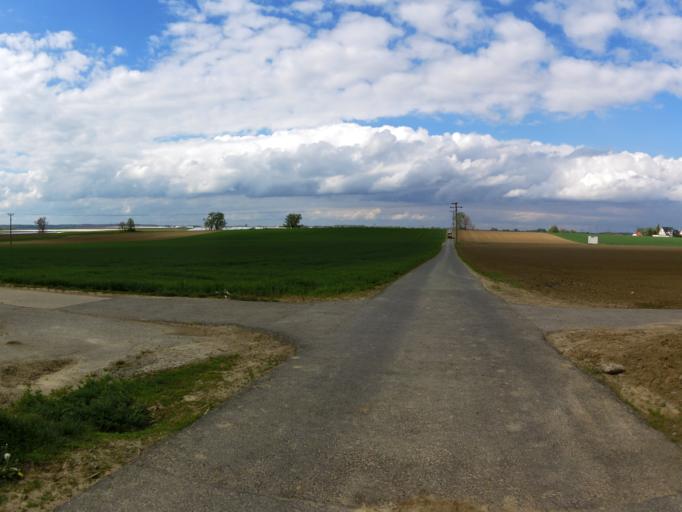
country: DE
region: Bavaria
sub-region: Regierungsbezirk Unterfranken
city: Oberpleichfeld
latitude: 49.8724
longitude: 10.0795
